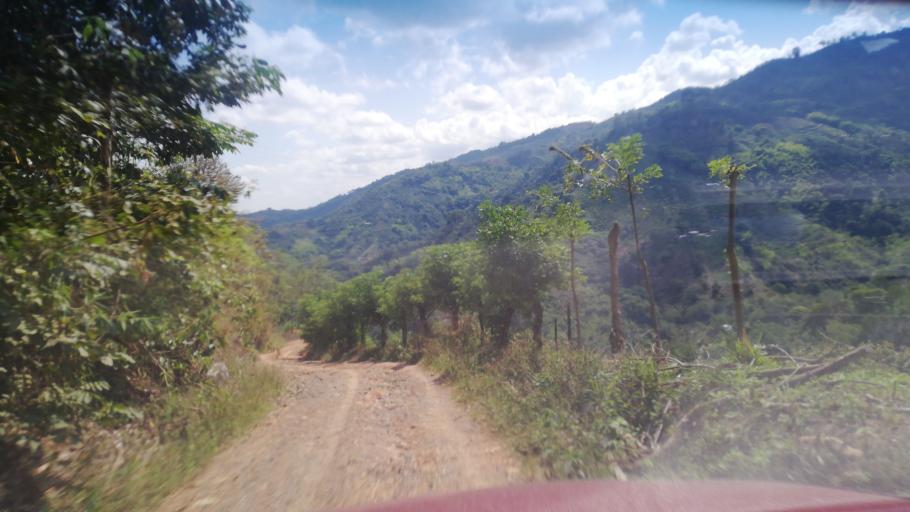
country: CO
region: Risaralda
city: Balboa
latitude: 4.9191
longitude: -75.9517
